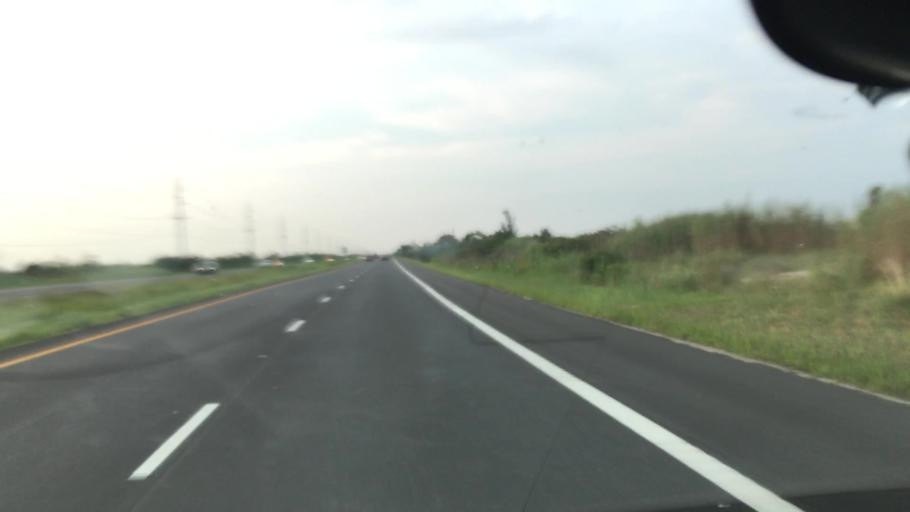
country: US
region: Delaware
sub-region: Sussex County
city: Long Neck
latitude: 38.6289
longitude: -75.0675
